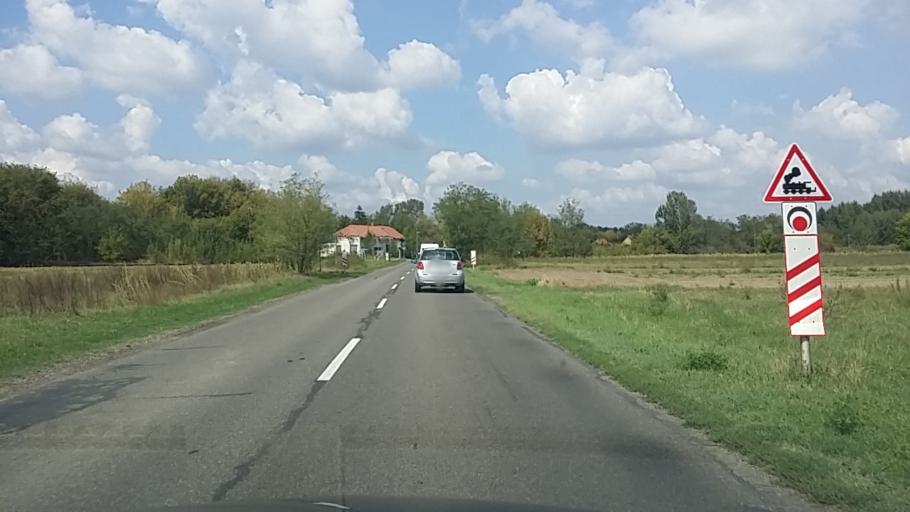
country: HU
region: Bacs-Kiskun
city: Tiszaalpar
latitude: 46.8324
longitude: 19.9740
